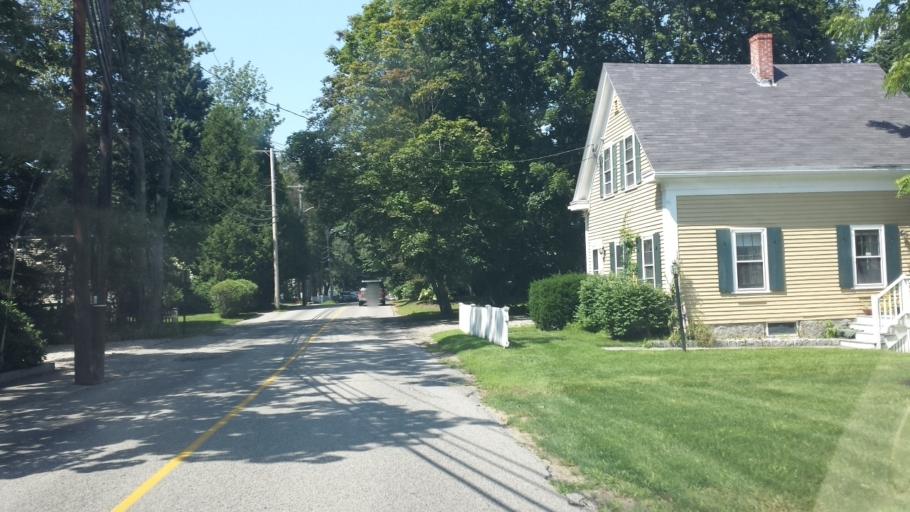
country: US
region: Maine
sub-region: York County
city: Kennebunkport
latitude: 43.3585
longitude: -70.4722
